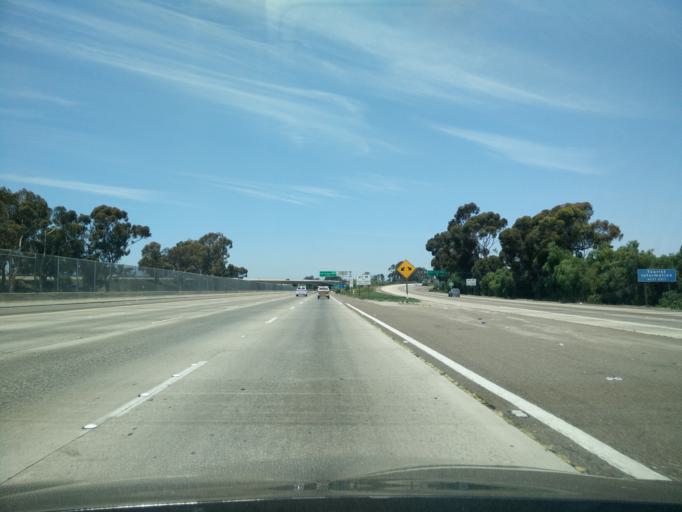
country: MX
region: Baja California
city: Tijuana
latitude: 32.5472
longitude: -117.0366
